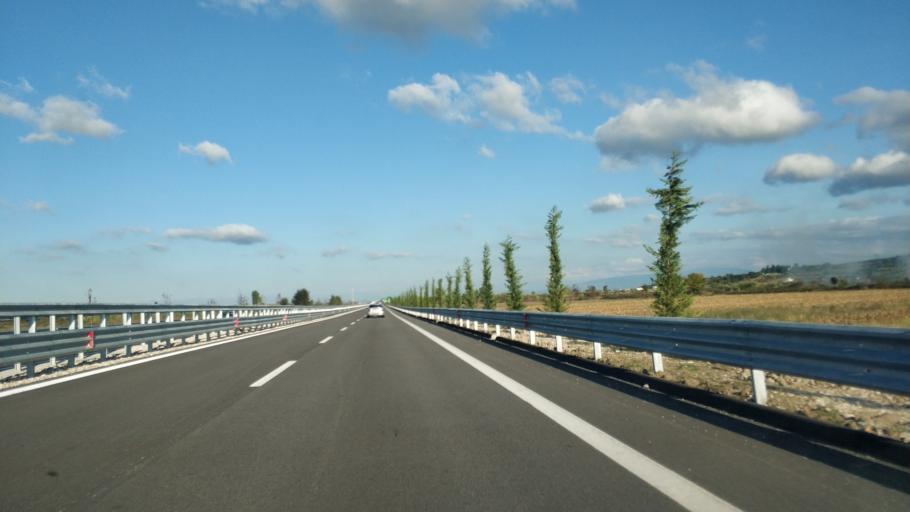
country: AL
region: Fier
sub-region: Rrethi i Fierit
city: Topoje
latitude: 40.7378
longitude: 19.4576
